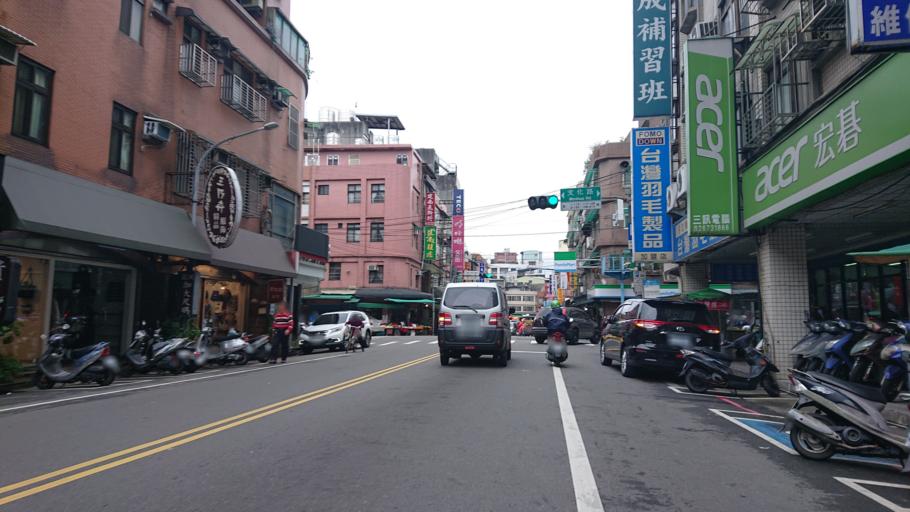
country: TW
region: Taiwan
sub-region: Taoyuan
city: Taoyuan
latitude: 24.9365
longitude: 121.3702
